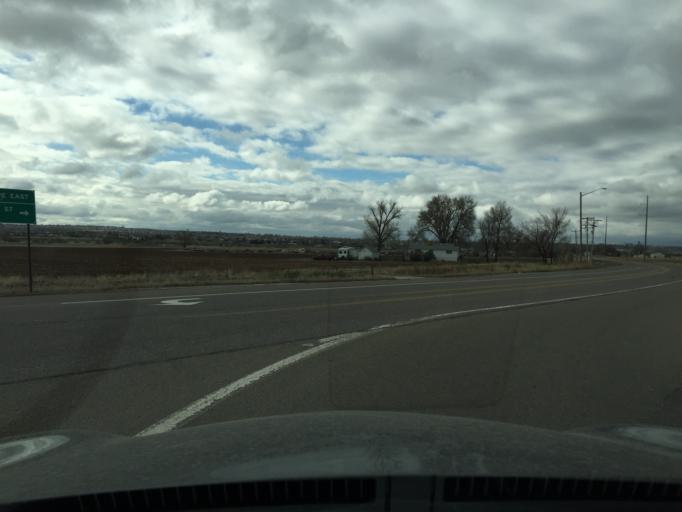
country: US
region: Colorado
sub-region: Adams County
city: Northglenn
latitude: 39.9691
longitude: -104.9781
